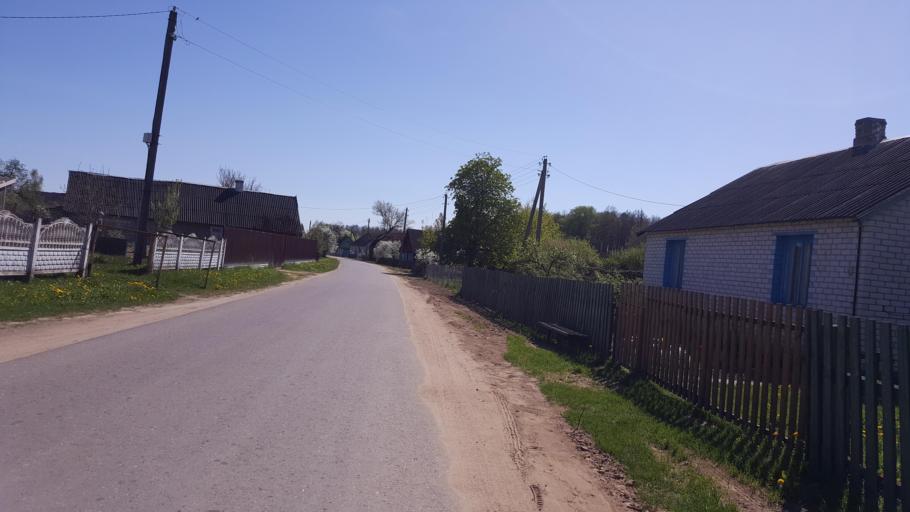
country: BY
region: Brest
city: Kamyanyets
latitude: 52.4442
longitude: 23.8448
